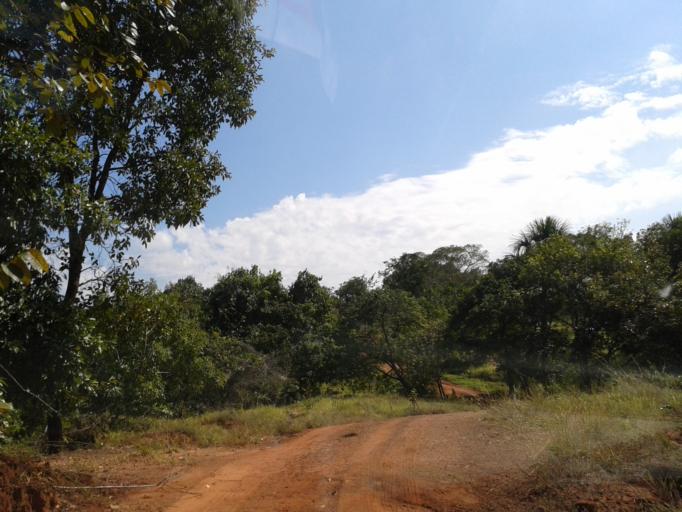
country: BR
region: Minas Gerais
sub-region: Campina Verde
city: Campina Verde
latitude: -19.3862
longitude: -49.6613
